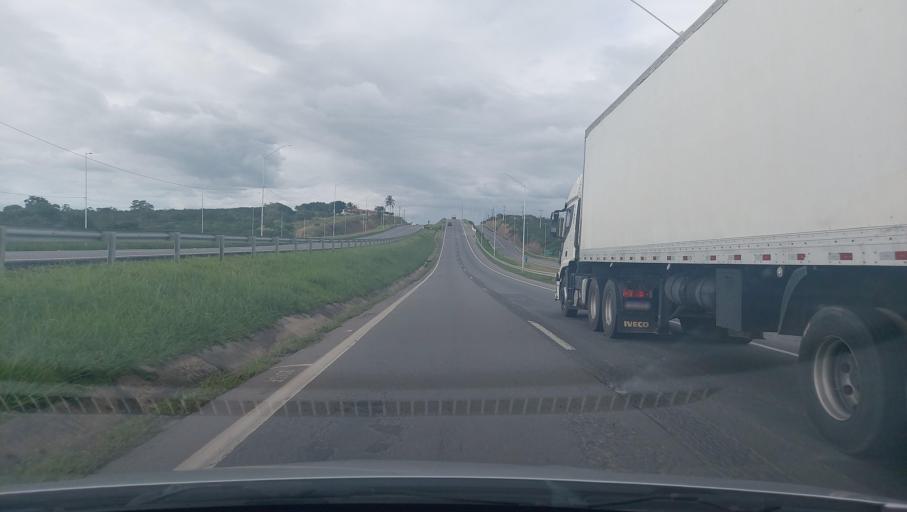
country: BR
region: Bahia
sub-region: Santo Estevao
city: Santo Estevao
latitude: -12.3904
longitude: -39.1446
